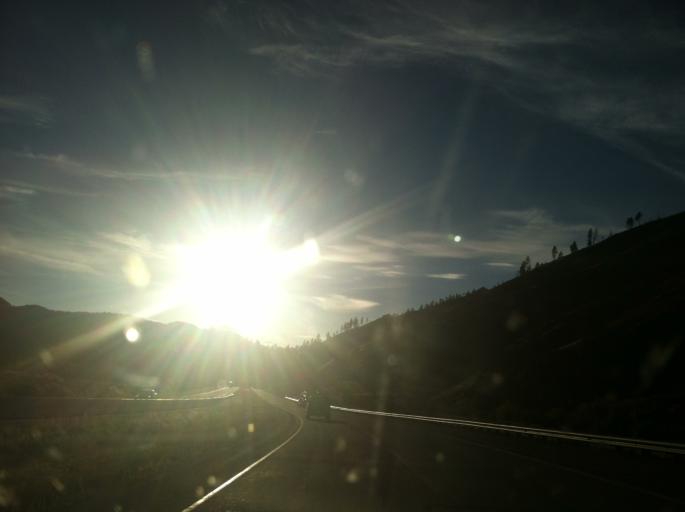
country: US
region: Montana
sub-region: Missoula County
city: Clinton
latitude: 46.7046
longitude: -113.4584
